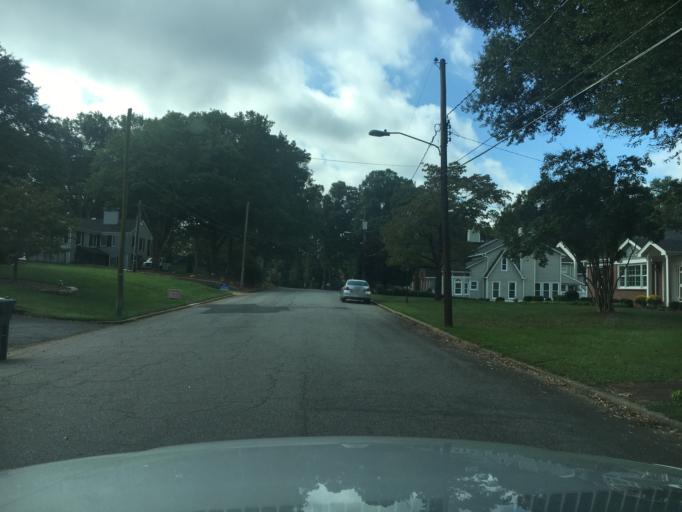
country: US
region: North Carolina
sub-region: Catawba County
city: Hickory
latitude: 35.7462
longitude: -81.3380
